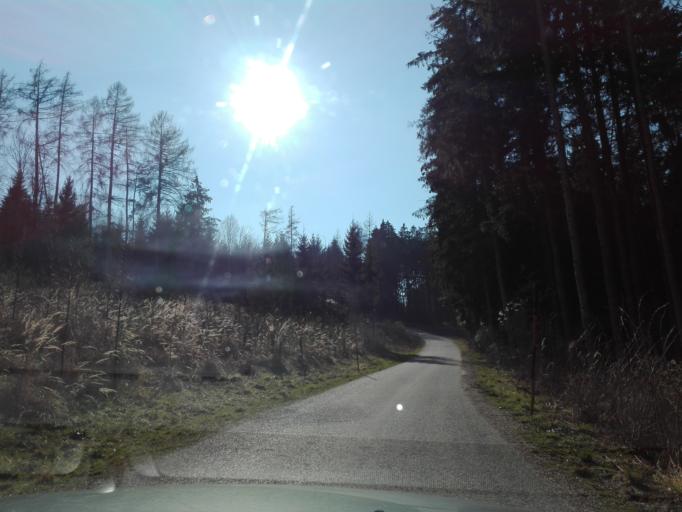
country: AT
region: Upper Austria
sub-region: Wels-Land
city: Holzhausen
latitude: 48.2522
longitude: 14.0706
